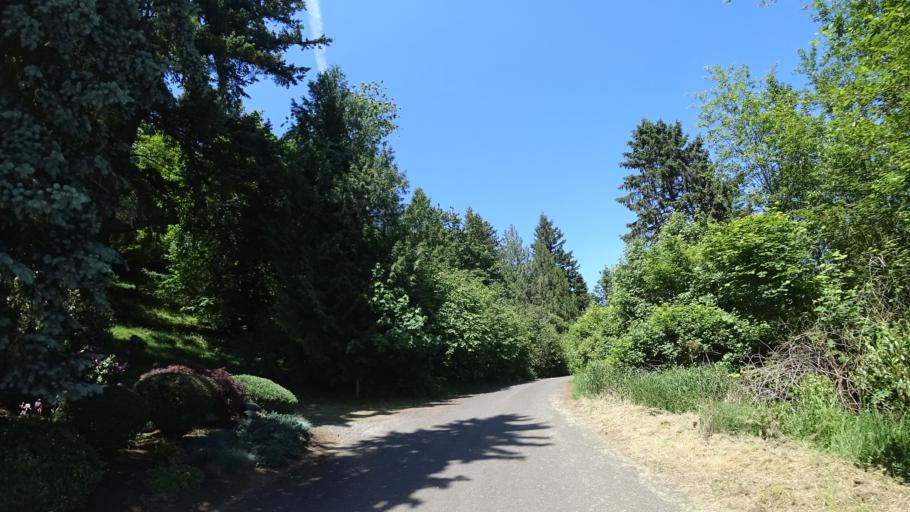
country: US
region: Oregon
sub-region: Clackamas County
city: Happy Valley
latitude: 45.4831
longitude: -122.4921
